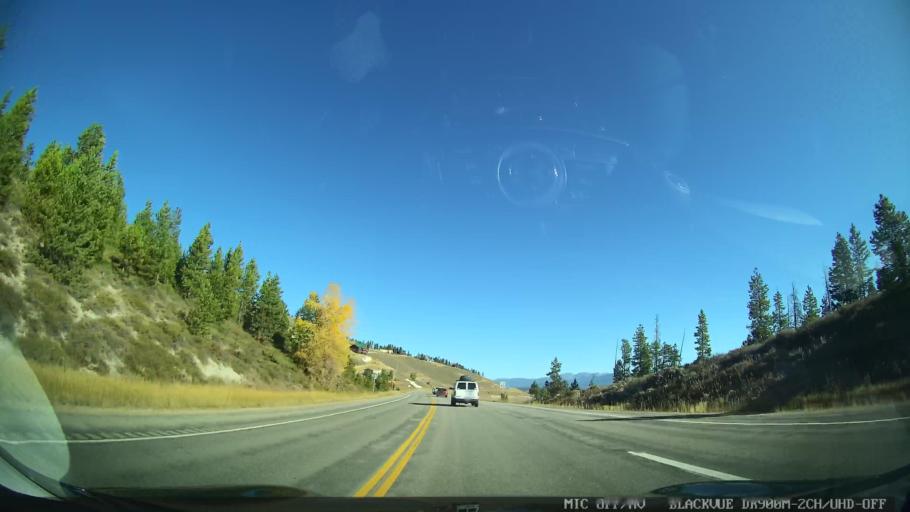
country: US
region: Colorado
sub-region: Grand County
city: Granby
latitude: 40.1432
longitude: -105.8906
